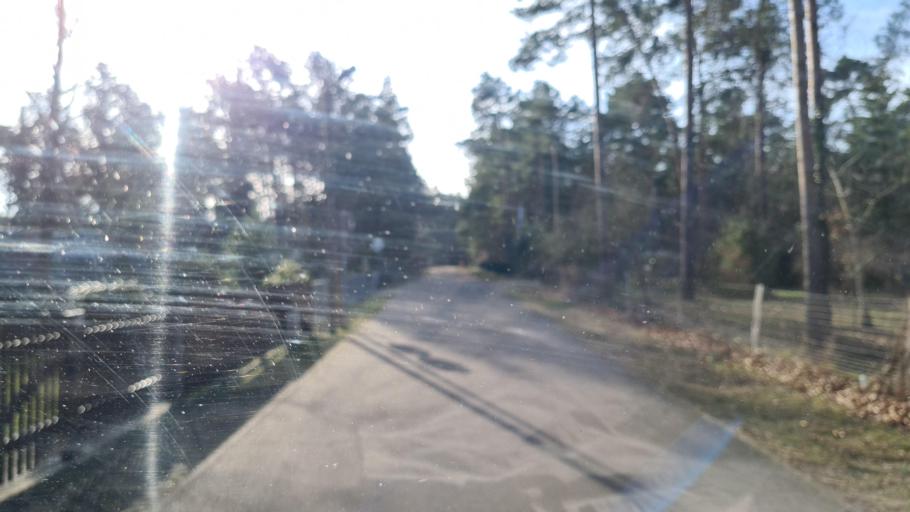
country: DE
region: Brandenburg
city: Gross Koris
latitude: 52.1612
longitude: 13.6894
